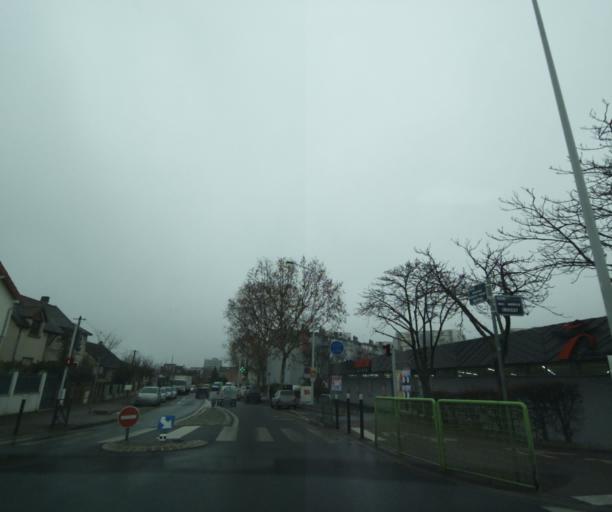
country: FR
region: Ile-de-France
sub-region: Departement des Hauts-de-Seine
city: Nanterre
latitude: 48.8961
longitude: 2.2081
